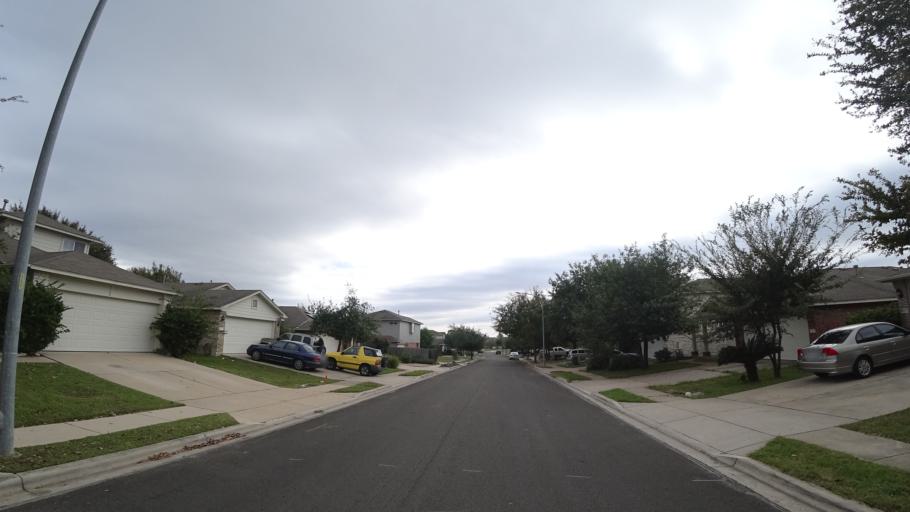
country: US
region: Texas
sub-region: Travis County
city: Manchaca
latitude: 30.1520
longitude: -97.8441
